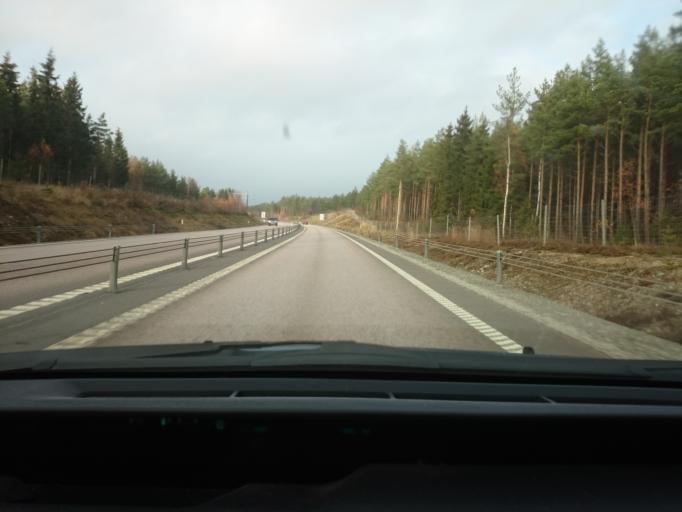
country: SE
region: Vaestmanland
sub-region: Sala Kommun
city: Sala
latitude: 59.9269
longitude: 16.5247
